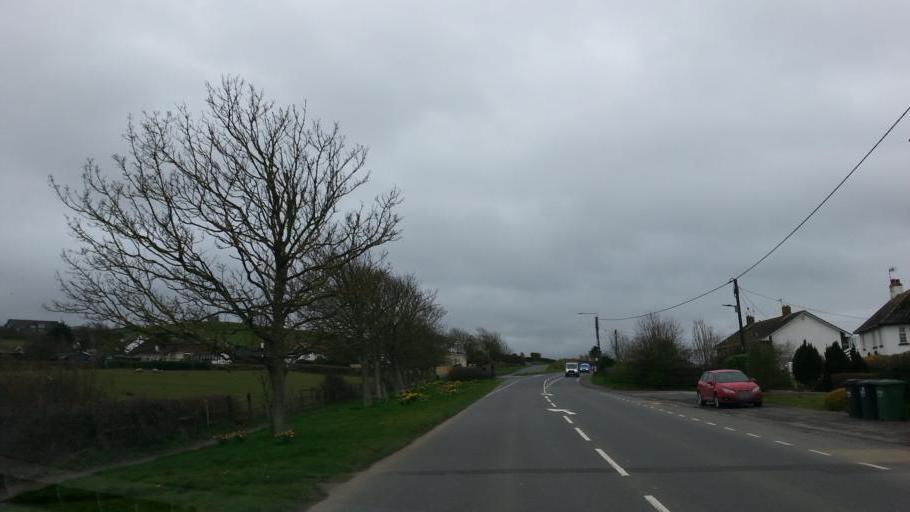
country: GB
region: England
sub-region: Devon
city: Appledore
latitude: 51.0623
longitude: -4.1660
